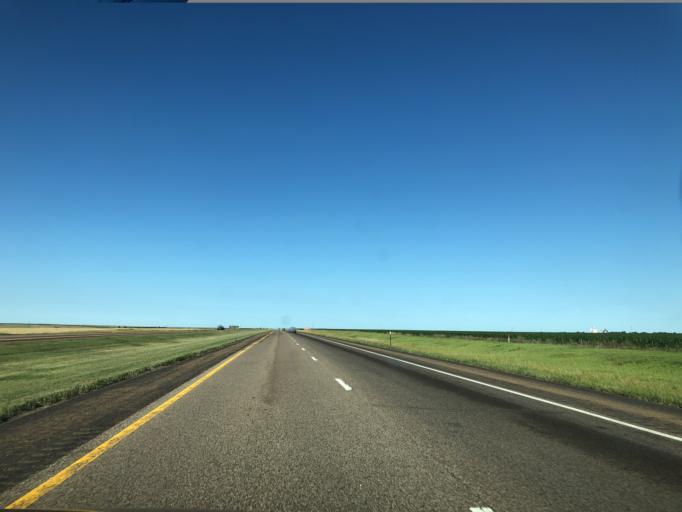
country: US
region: Kansas
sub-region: Thomas County
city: Colby
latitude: 39.3617
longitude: -101.3261
